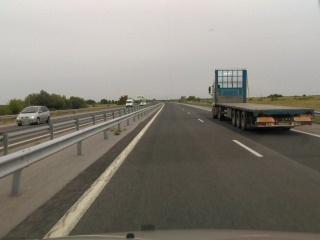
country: BG
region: Stara Zagora
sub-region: Obshtina Stara Zagora
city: Stara Zagora
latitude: 42.3234
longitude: 25.5986
